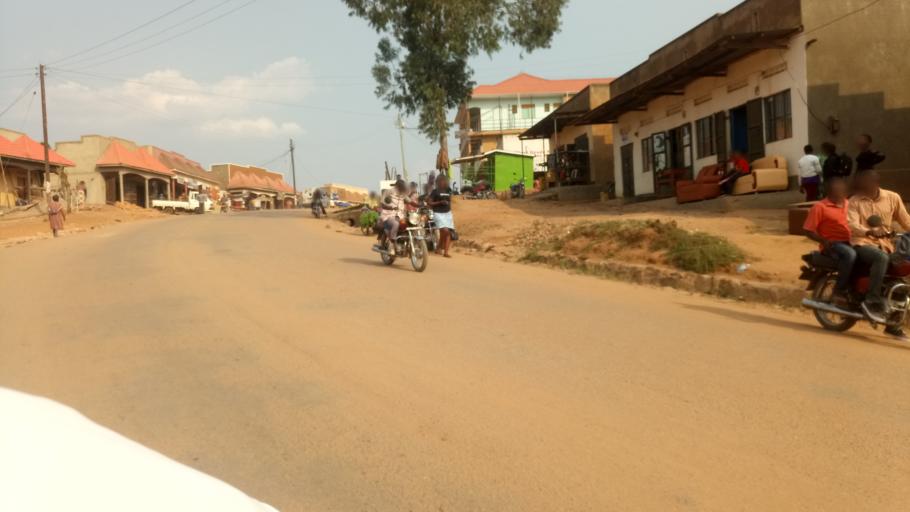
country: UG
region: Western Region
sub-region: Mbarara District
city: Mbarara
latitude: -0.6179
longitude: 30.6690
